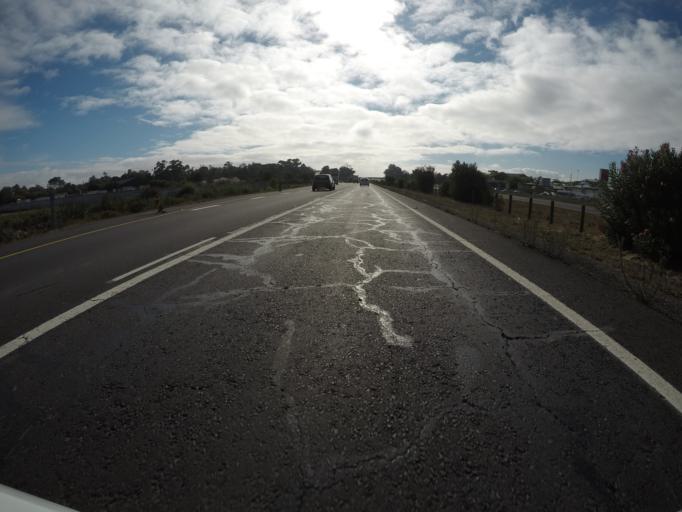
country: ZA
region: Western Cape
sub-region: City of Cape Town
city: Kraaifontein
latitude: -33.8368
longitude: 18.7305
